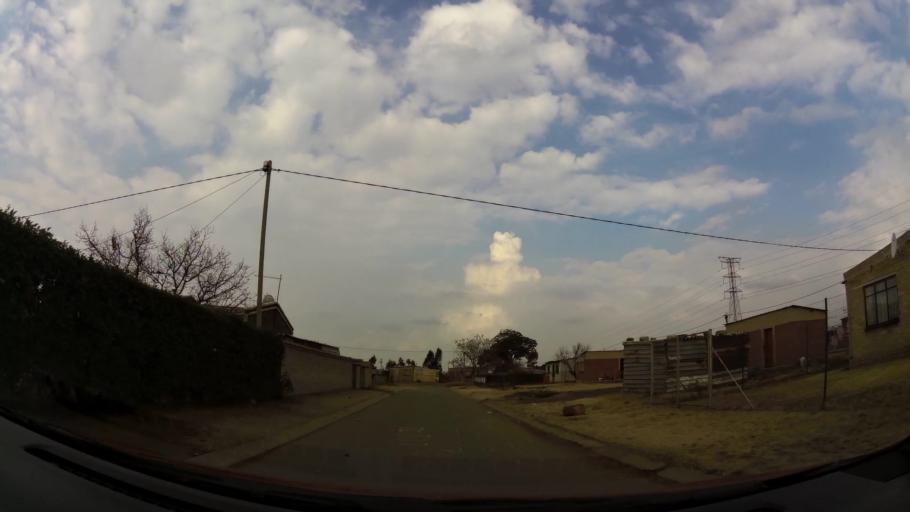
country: ZA
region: Gauteng
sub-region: Sedibeng District Municipality
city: Vanderbijlpark
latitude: -26.6771
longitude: 27.8581
